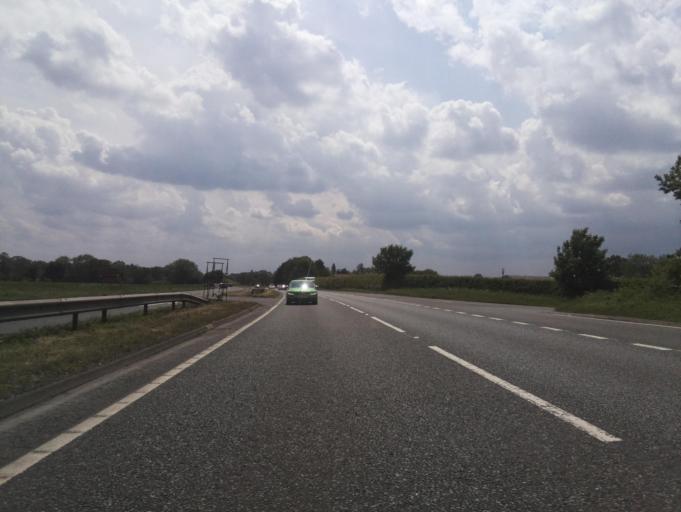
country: GB
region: England
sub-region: North Yorkshire
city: Thirsk
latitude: 54.2628
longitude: -1.3486
